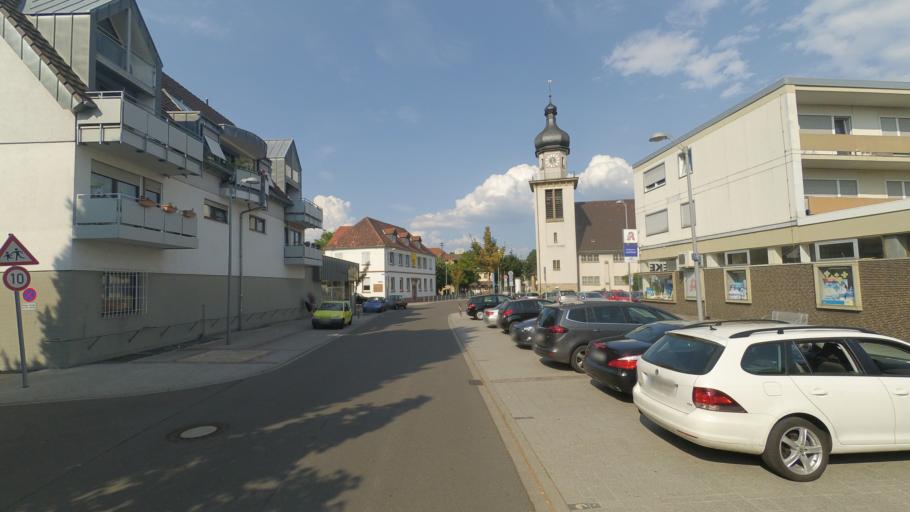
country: DE
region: Rheinland-Pfalz
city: Frankenthal
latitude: 49.5293
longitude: 8.3912
